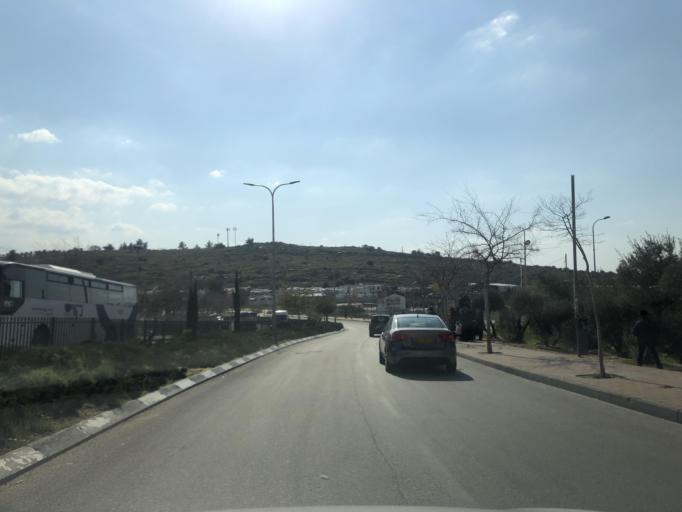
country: IL
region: Jerusalem
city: Modiin Ilit
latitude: 31.9359
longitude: 35.0381
